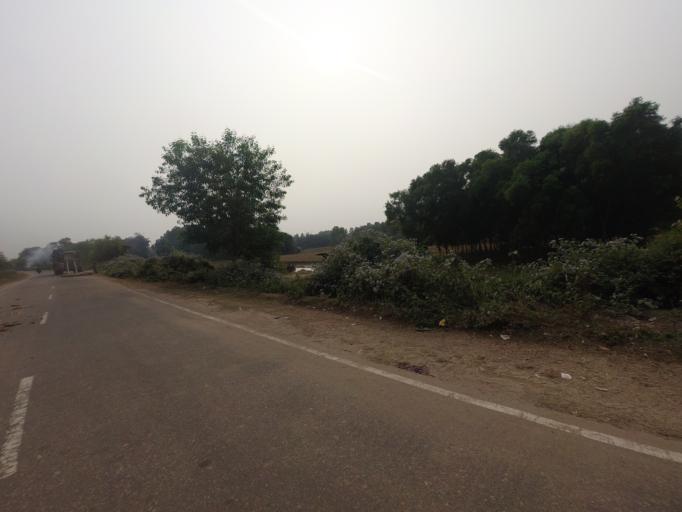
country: BD
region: Dhaka
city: Netrakona
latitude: 25.1728
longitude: 90.6565
